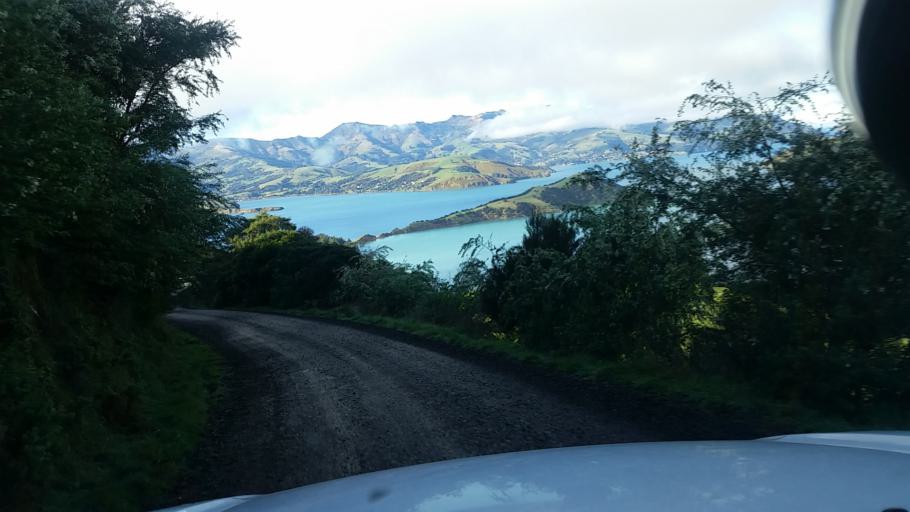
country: NZ
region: Canterbury
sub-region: Christchurch City
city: Christchurch
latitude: -43.7523
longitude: 172.9100
